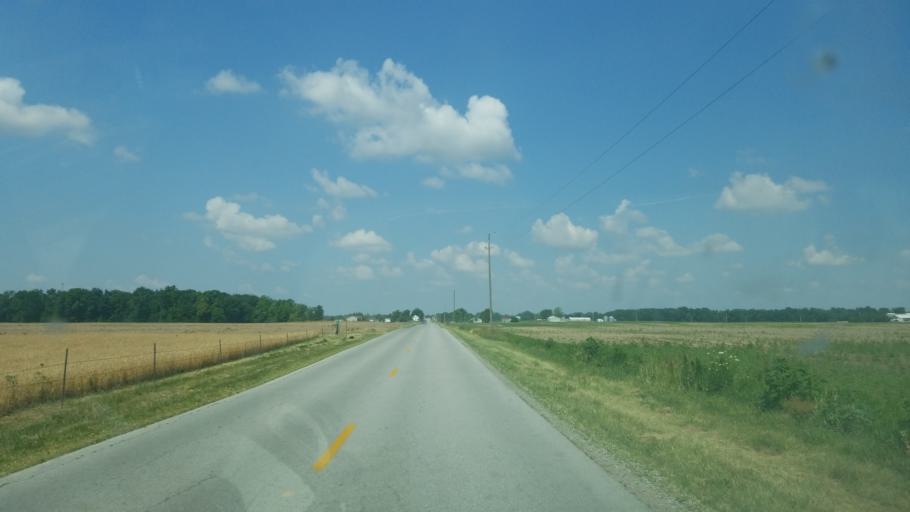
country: US
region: Ohio
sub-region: Auglaize County
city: Wapakoneta
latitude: 40.5702
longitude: -84.1515
